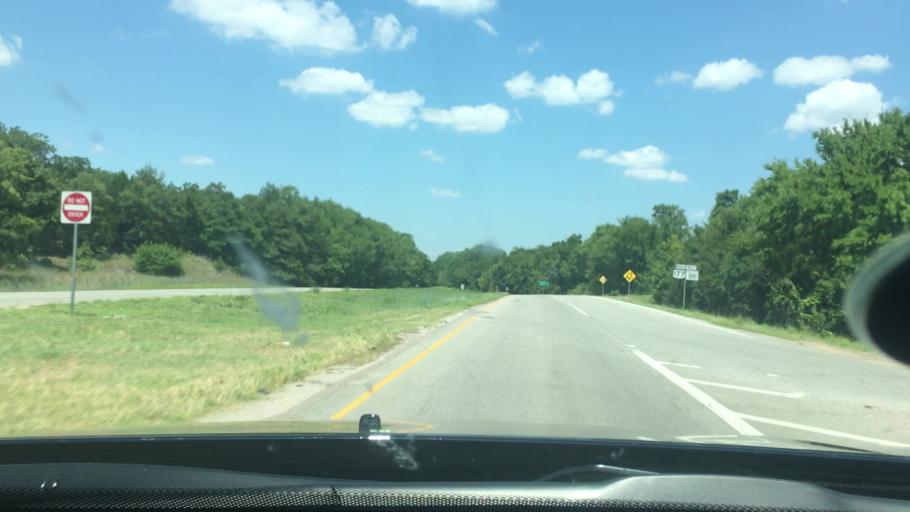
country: US
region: Oklahoma
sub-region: Marshall County
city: Oakland
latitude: 34.1699
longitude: -96.8339
